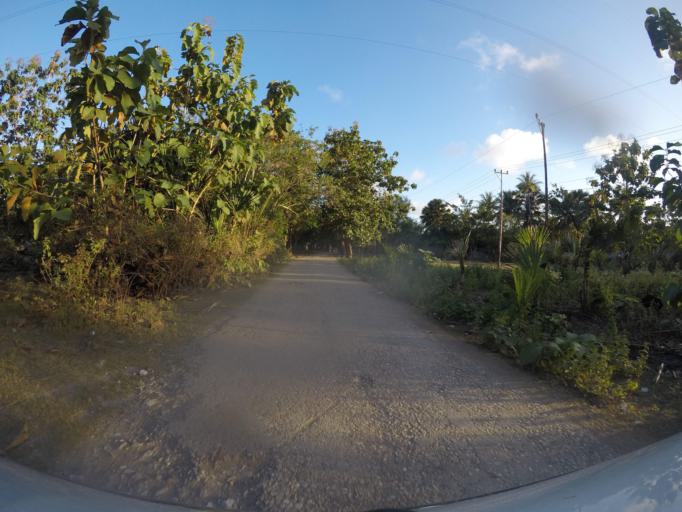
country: TL
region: Baucau
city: Venilale
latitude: -8.7386
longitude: 126.7147
